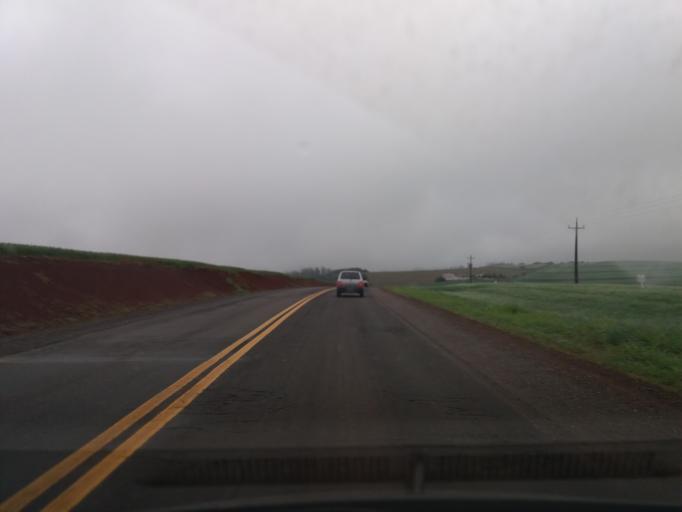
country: BR
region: Parana
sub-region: Realeza
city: Realeza
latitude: -25.8305
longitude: -53.5196
